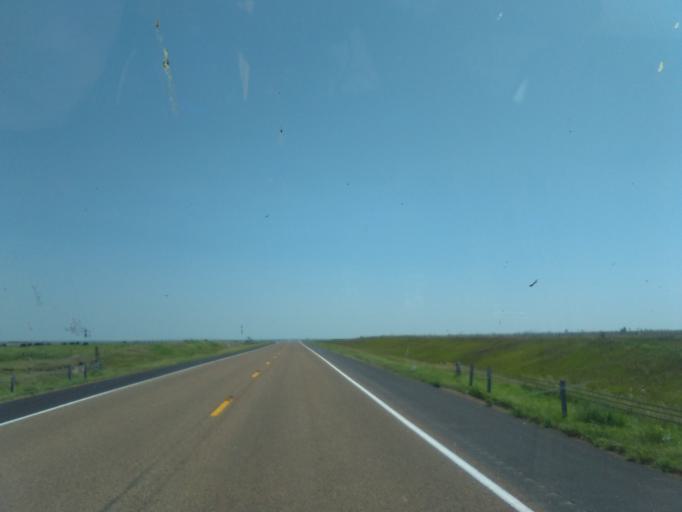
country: US
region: Nebraska
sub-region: Hitchcock County
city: Trenton
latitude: 40.2284
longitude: -100.9214
